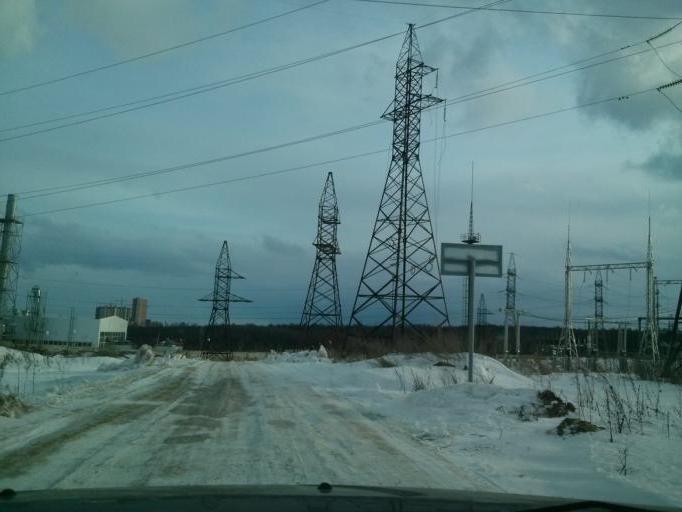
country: RU
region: Nizjnij Novgorod
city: Afonino
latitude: 56.2652
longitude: 44.0309
